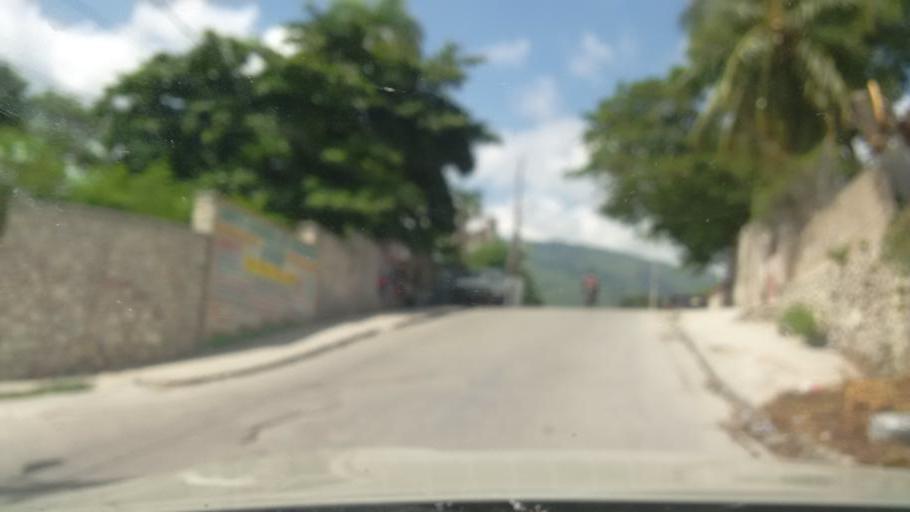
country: HT
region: Ouest
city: Delmas 73
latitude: 18.5404
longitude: -72.3183
